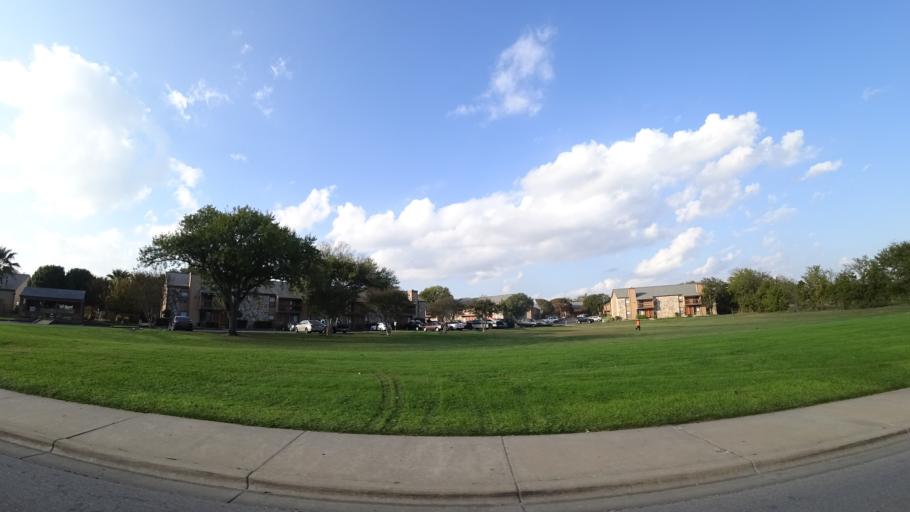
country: US
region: Texas
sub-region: Williamson County
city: Round Rock
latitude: 30.4958
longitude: -97.6678
